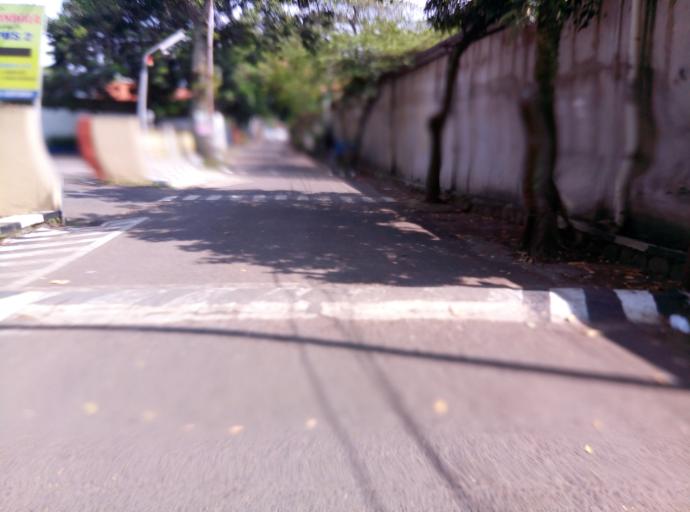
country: ID
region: West Java
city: Bandung
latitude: -6.9436
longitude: 107.6442
